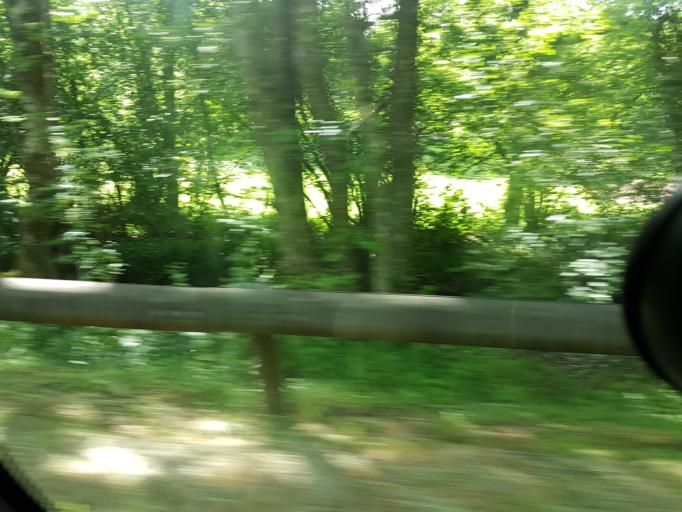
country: FR
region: Bourgogne
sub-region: Departement de la Cote-d'Or
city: Saulieu
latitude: 47.1526
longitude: 4.1890
